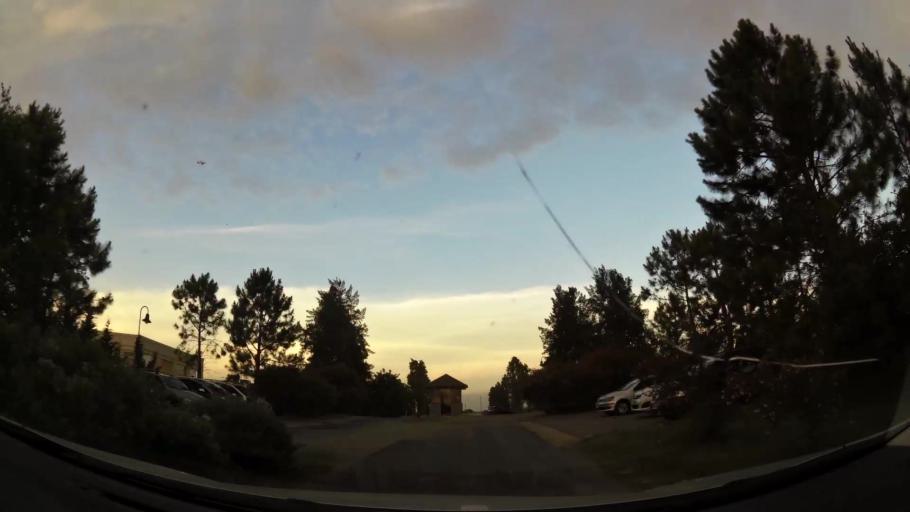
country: AR
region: Buenos Aires
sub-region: Partido de Tigre
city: Tigre
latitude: -34.4399
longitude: -58.6478
